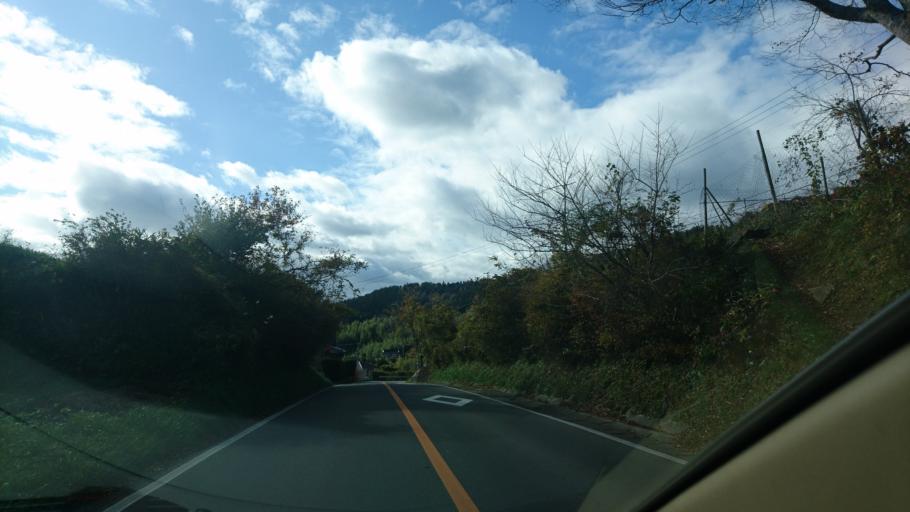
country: JP
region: Iwate
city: Ofunato
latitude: 39.0047
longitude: 141.7092
